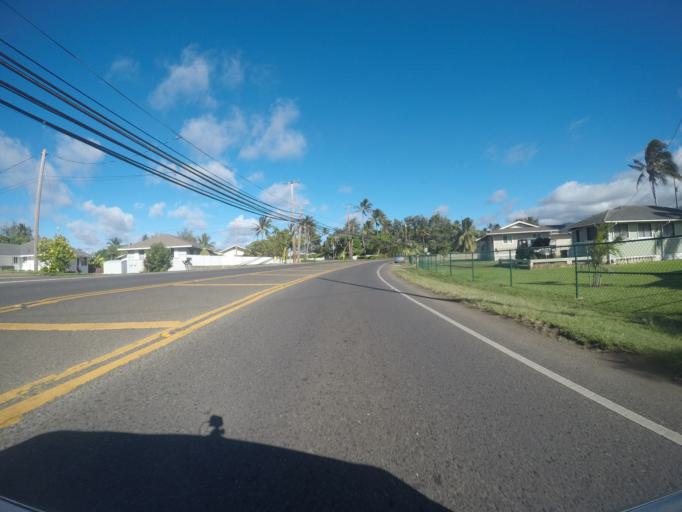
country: US
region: Hawaii
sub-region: Honolulu County
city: La'ie
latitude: 21.6466
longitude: -157.9204
